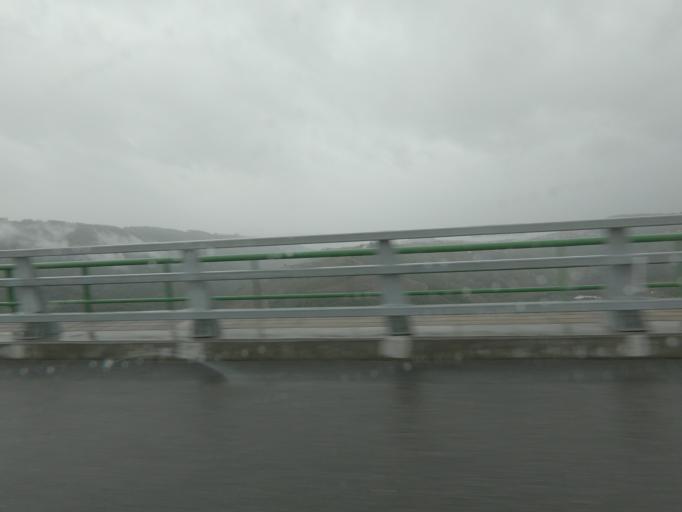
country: PT
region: Viana do Castelo
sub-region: Ponte de Lima
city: Ponte de Lima
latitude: 41.7358
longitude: -8.6203
